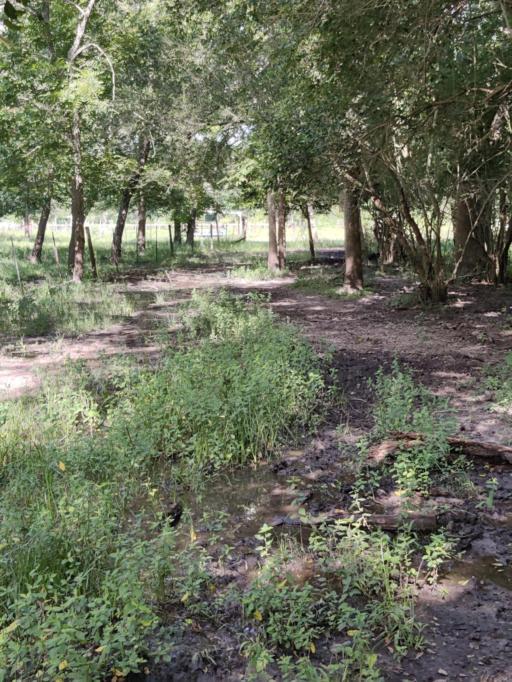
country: US
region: Texas
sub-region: Harris County
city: Oak Cliff Place
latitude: 29.8325
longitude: -95.6643
